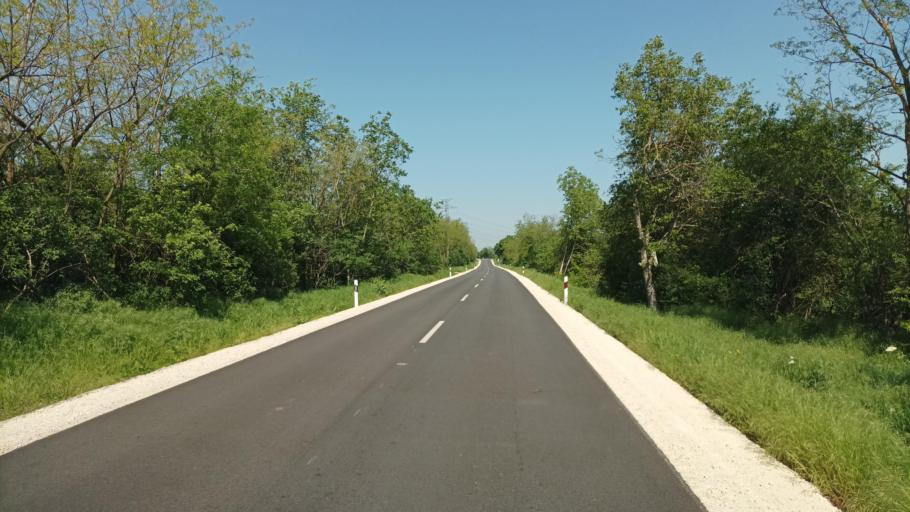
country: HU
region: Pest
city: Gomba
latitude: 47.3815
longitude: 19.5099
